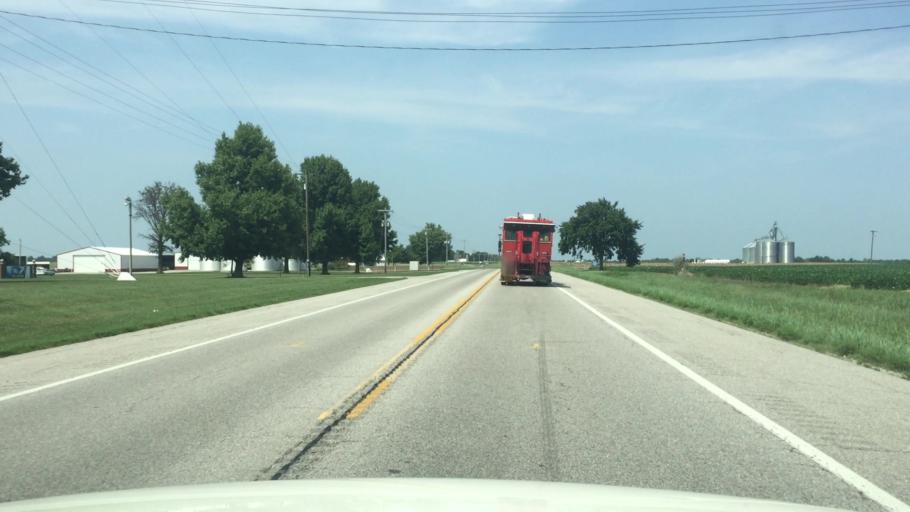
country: US
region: Missouri
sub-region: Jasper County
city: Carl Junction
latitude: 37.2201
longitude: -94.7049
